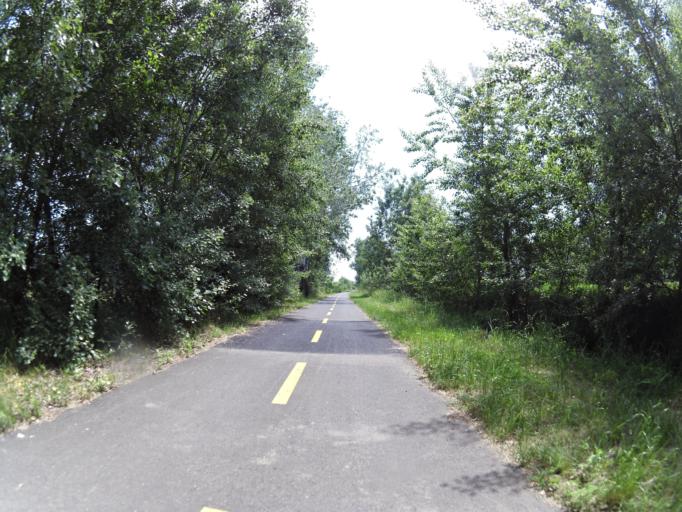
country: HU
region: Csongrad
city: Kistelek
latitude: 46.4568
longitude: 19.9924
